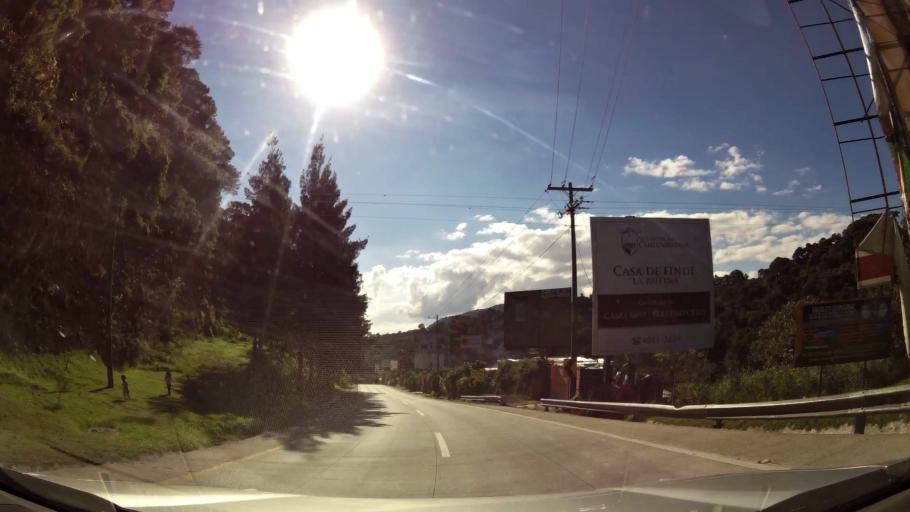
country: GT
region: Sacatepequez
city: Santa Lucia Milpas Altas
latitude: 14.5759
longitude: -90.6841
